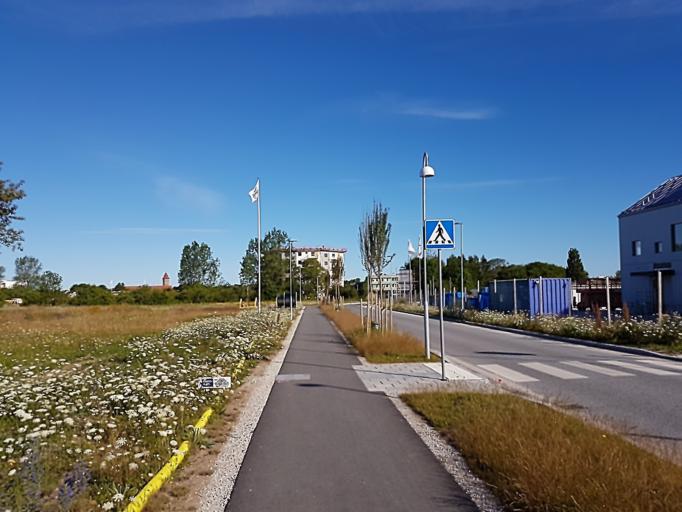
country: SE
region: Gotland
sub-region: Gotland
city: Visby
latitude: 57.6276
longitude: 18.3098
